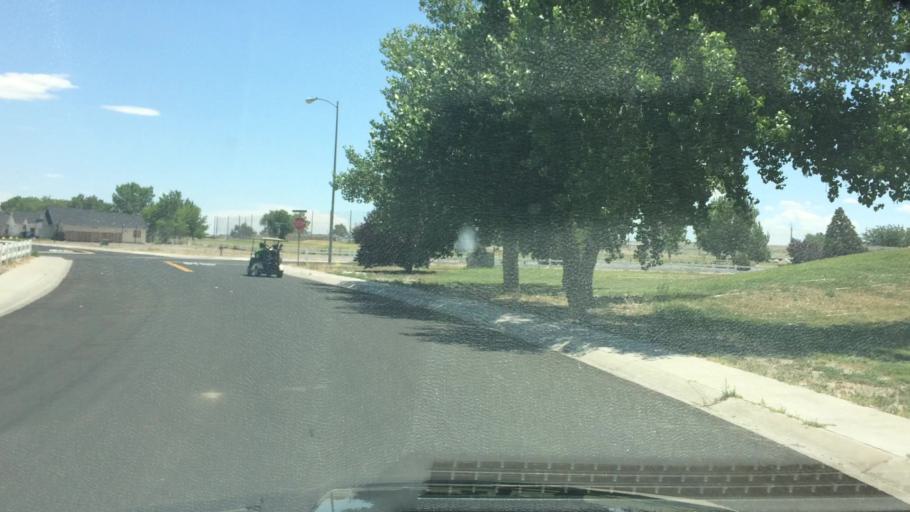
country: US
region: Nevada
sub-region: Lyon County
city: Fernley
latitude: 39.5847
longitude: -119.1510
